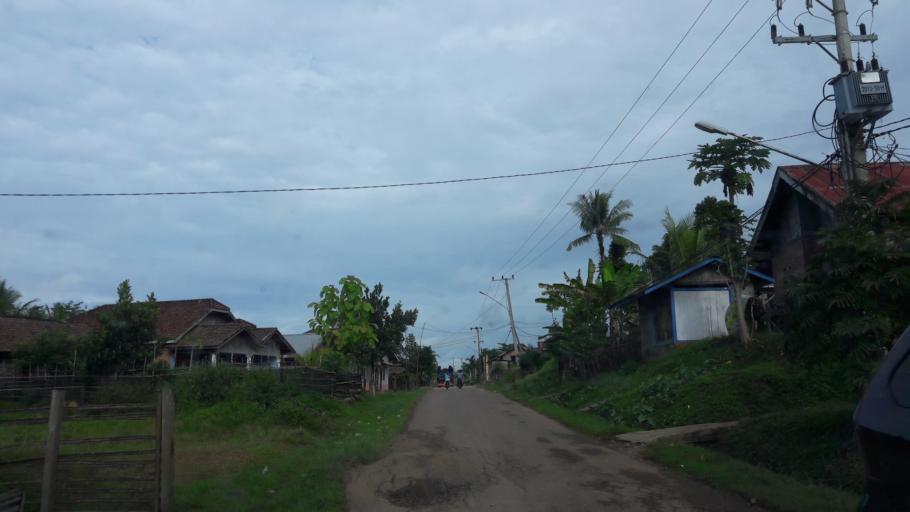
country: ID
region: South Sumatra
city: Gunungmegang Dalam
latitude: -3.2693
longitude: 103.8004
